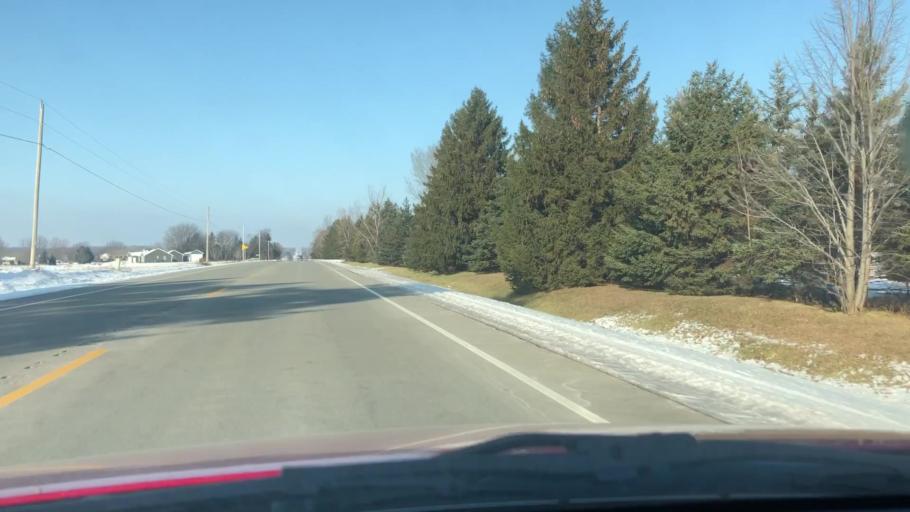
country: US
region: Wisconsin
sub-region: Outagamie County
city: Kimberly
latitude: 44.3472
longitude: -88.3749
